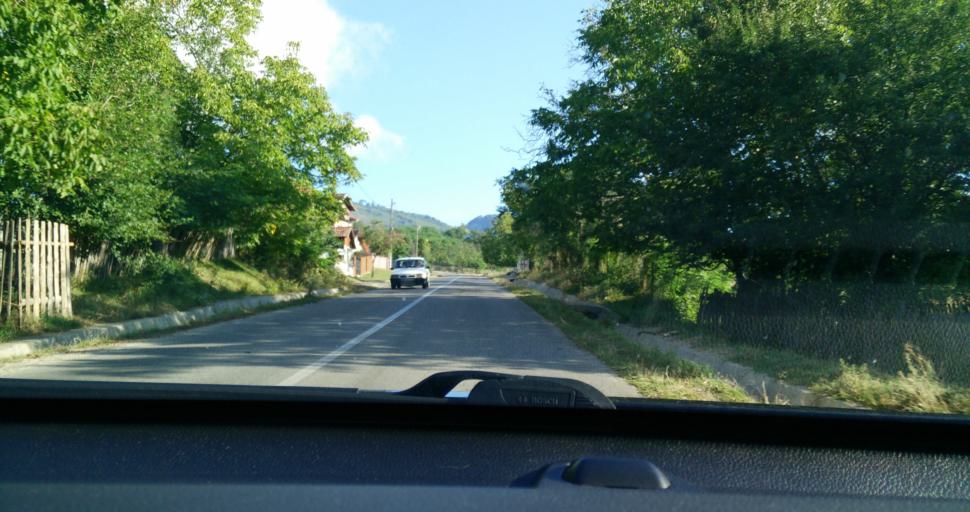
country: RO
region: Gorj
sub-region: Comuna Baia de Fier
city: Baia de Fier
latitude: 45.1751
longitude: 23.7812
